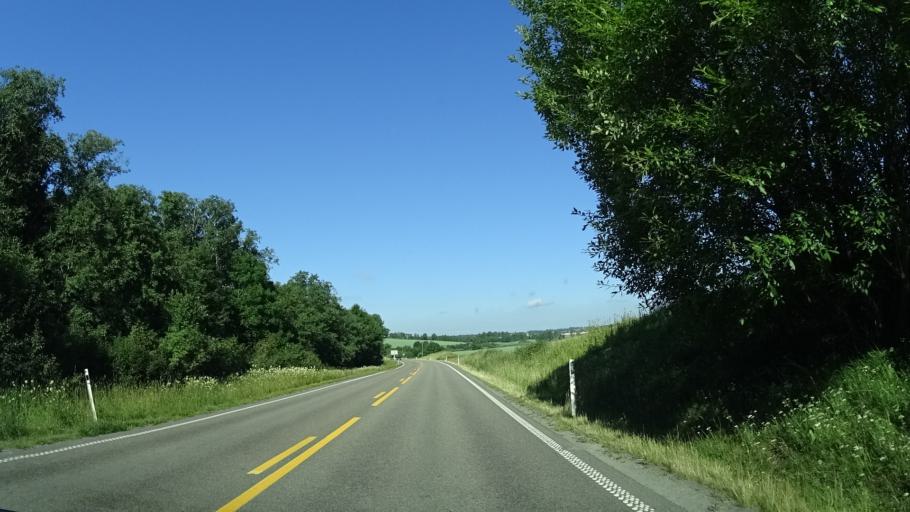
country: NO
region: Akershus
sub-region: Ski
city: Ski
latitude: 59.6845
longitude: 10.8399
